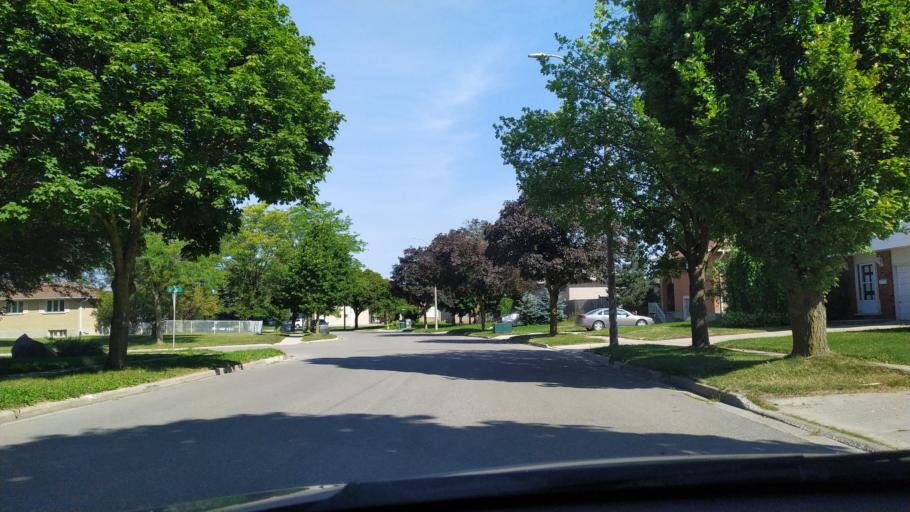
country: CA
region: Ontario
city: Stratford
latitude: 43.3858
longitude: -80.9675
